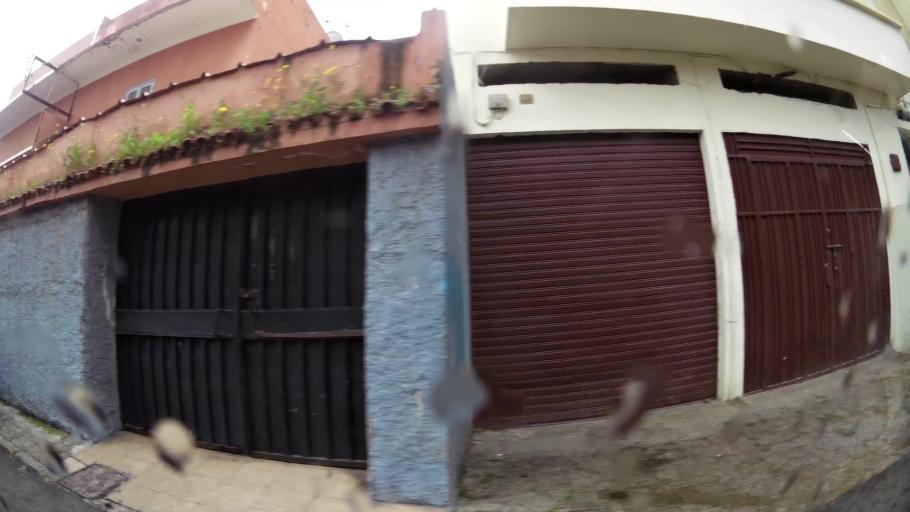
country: MA
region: Grand Casablanca
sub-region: Casablanca
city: Casablanca
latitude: 33.5745
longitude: -7.6270
